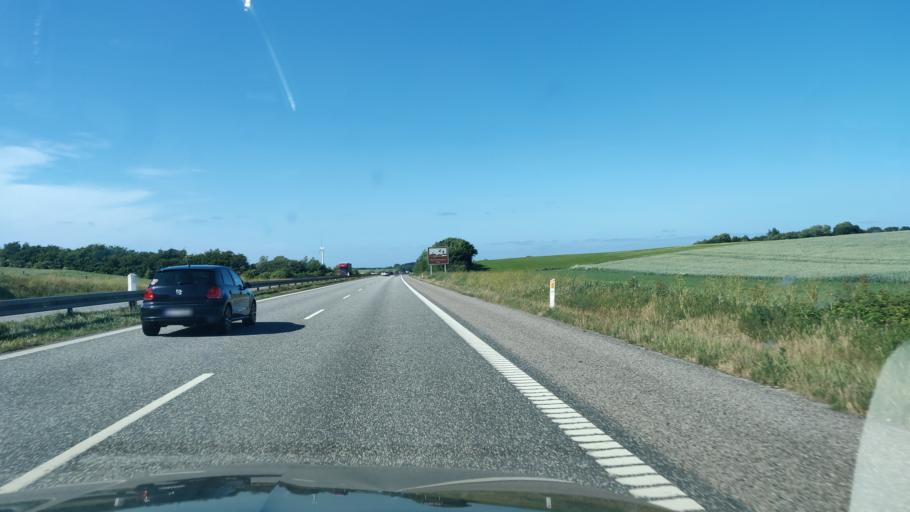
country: DK
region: North Denmark
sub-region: Mariagerfjord Kommune
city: Hobro
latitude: 56.7621
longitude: 9.6940
